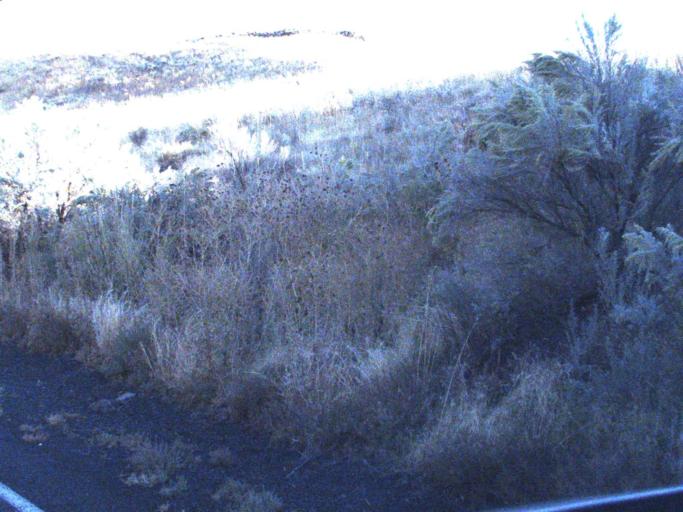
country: US
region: Washington
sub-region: Walla Walla County
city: Waitsburg
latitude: 46.6726
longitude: -118.3207
